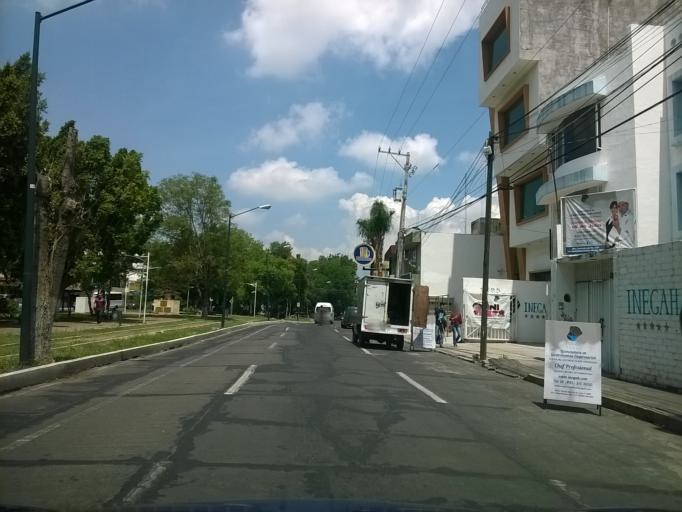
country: MX
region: Michoacan
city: Morelia
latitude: 19.6884
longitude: -101.1630
